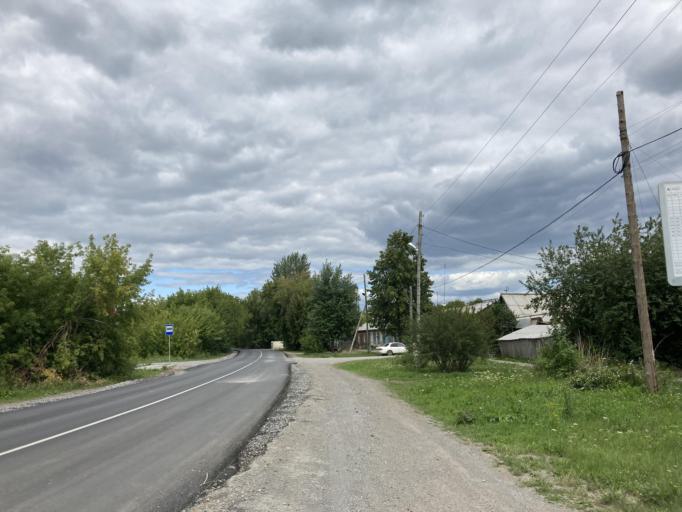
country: RU
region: Sverdlovsk
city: Bogdanovich
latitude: 56.7821
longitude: 62.0658
